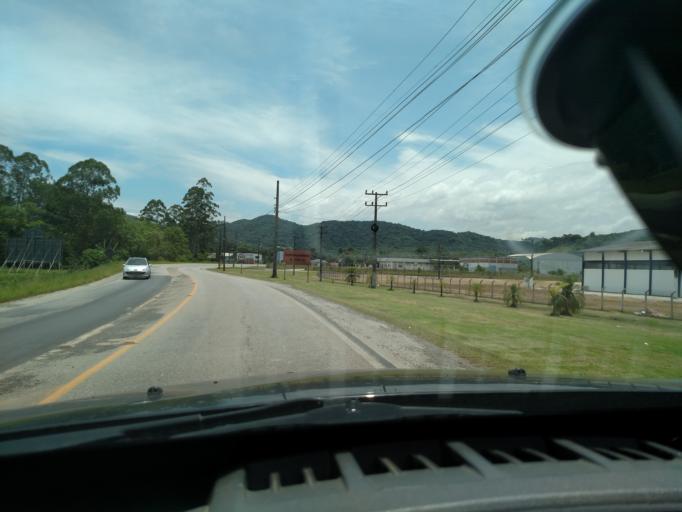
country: BR
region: Santa Catarina
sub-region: Gaspar
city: Gaspar
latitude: -26.9134
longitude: -48.9345
